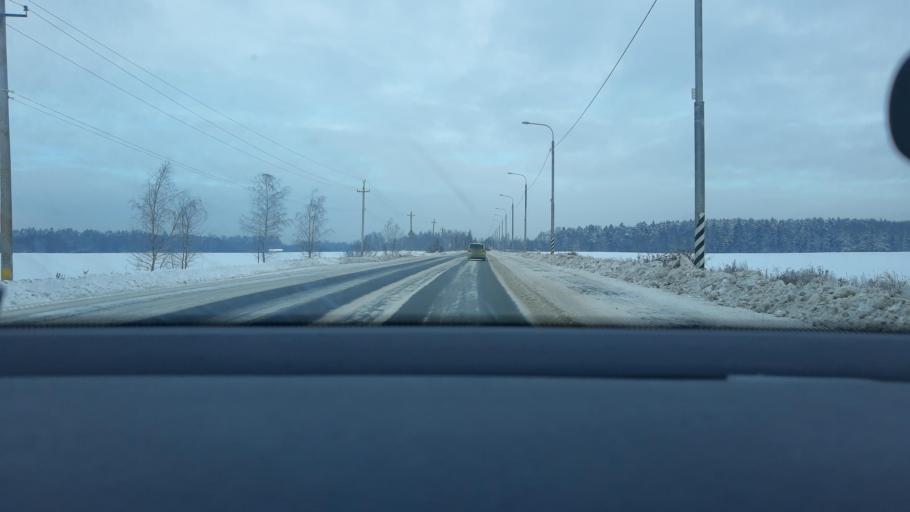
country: RU
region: Moskovskaya
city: Ivanteyevka
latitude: 56.0019
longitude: 37.9499
